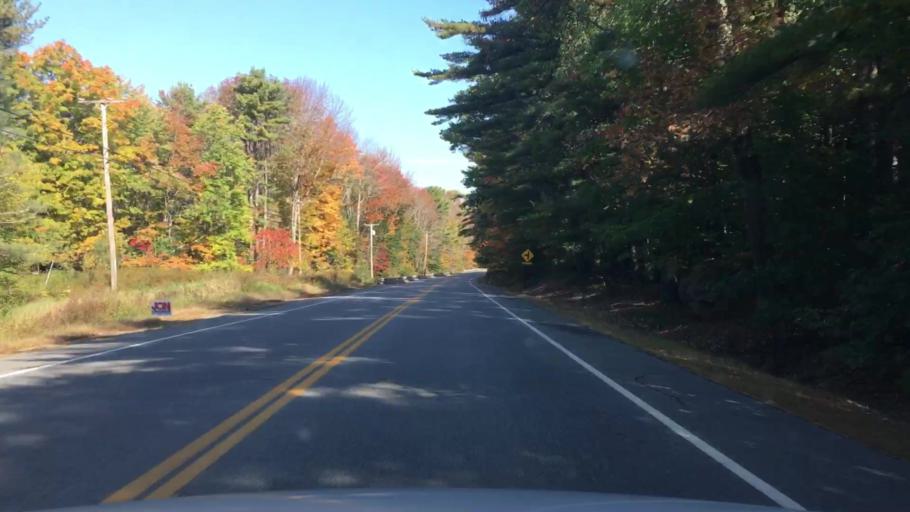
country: US
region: Maine
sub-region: Sagadahoc County
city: Topsham
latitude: 44.0051
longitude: -69.9489
